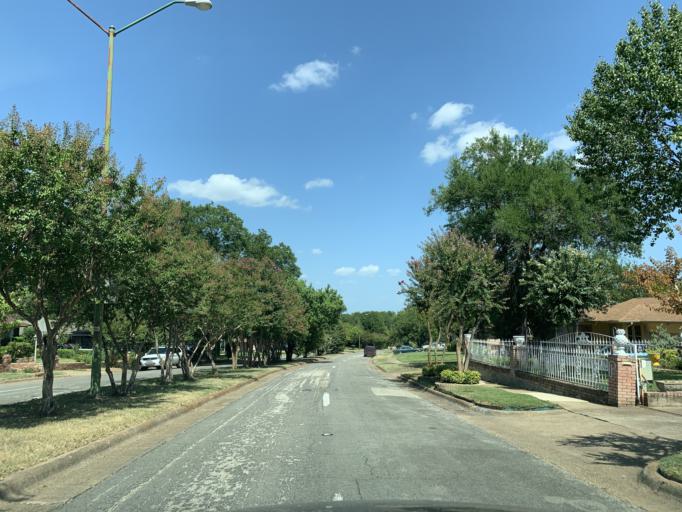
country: US
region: Texas
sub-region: Dallas County
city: Hutchins
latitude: 32.6756
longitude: -96.7963
